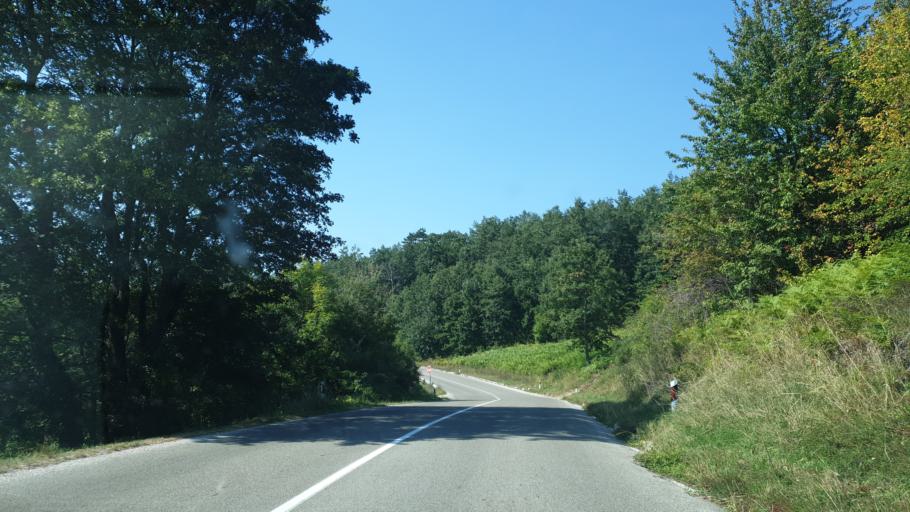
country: RS
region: Central Serbia
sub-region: Zlatiborski Okrug
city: Cajetina
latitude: 43.7227
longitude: 19.8135
